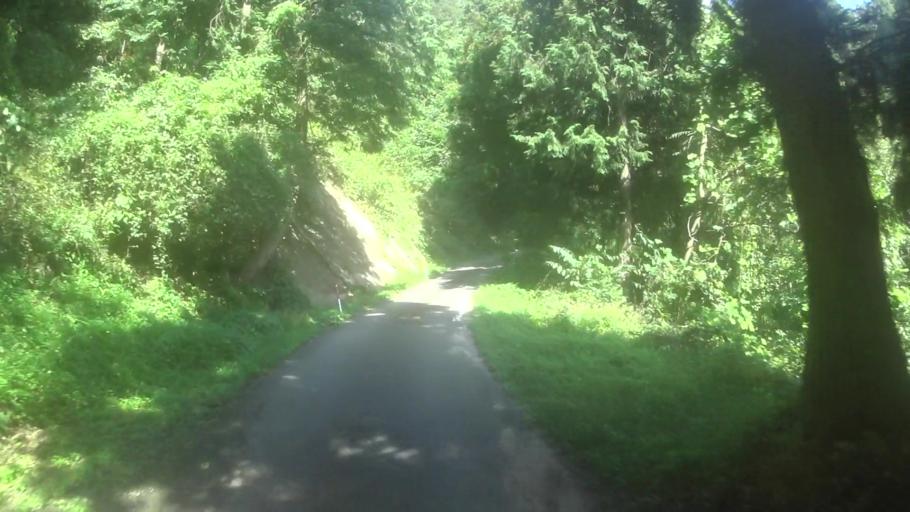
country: JP
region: Kyoto
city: Miyazu
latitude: 35.6654
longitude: 135.1295
